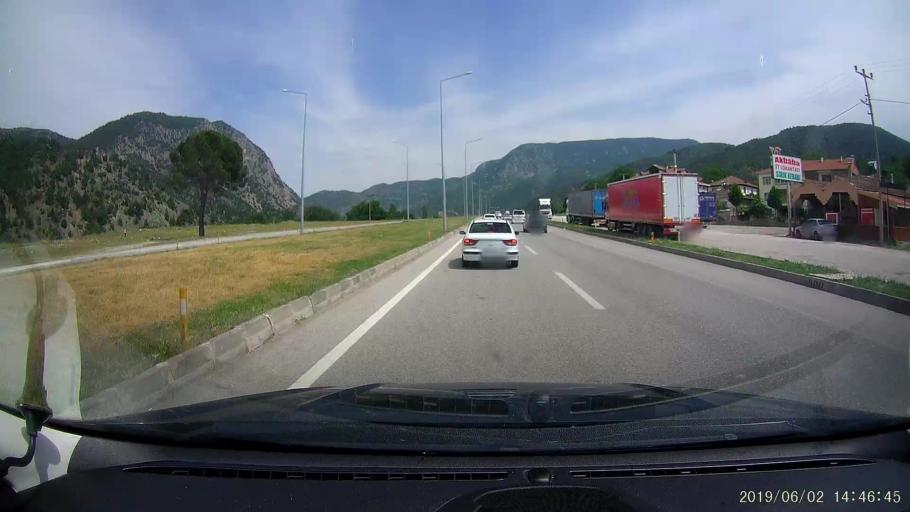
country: TR
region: Corum
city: Hacihamza
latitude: 41.0742
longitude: 34.4542
